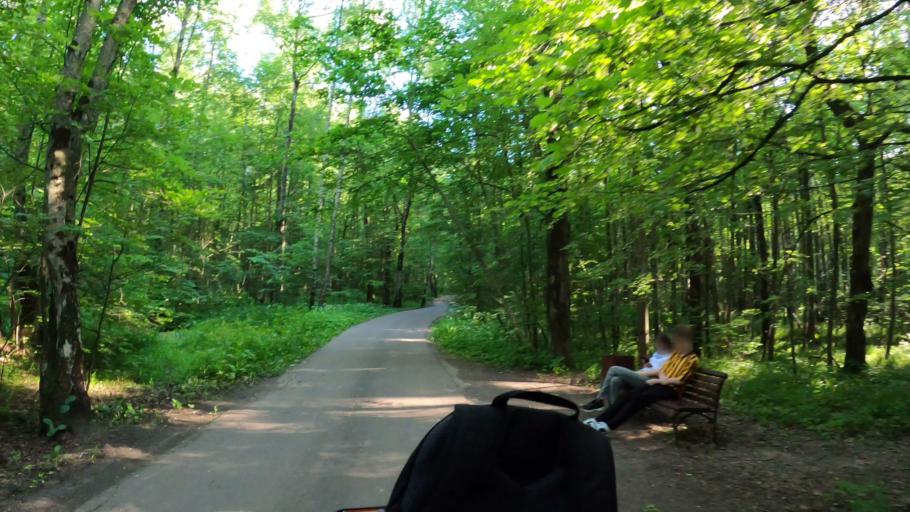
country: RU
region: Moscow
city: Zyuzino
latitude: 55.6195
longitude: 37.5608
